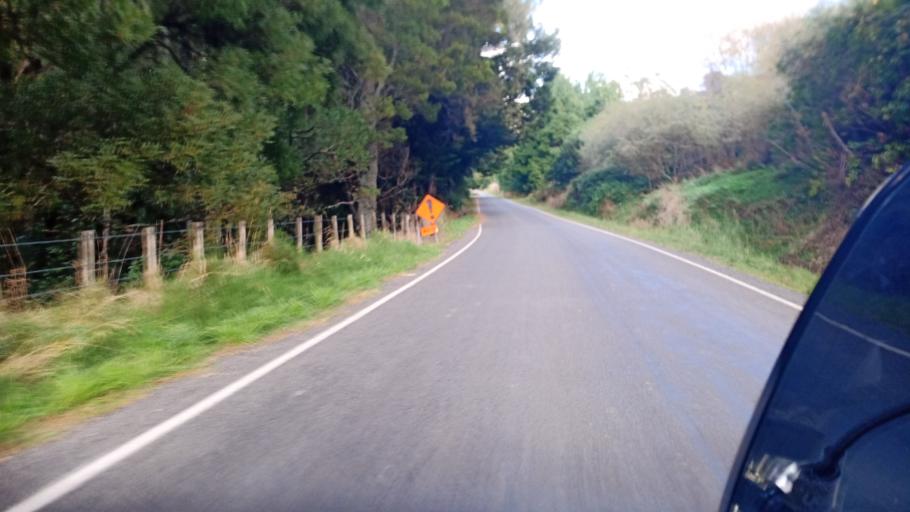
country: NZ
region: Gisborne
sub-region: Gisborne District
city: Gisborne
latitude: -38.5304
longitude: 177.5415
